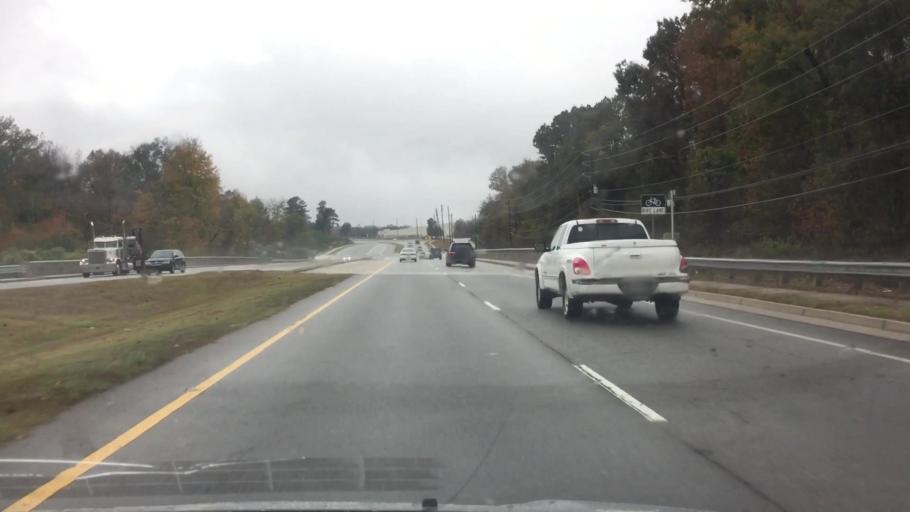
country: US
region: Georgia
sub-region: Henry County
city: Stockbridge
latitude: 33.5185
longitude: -84.1958
